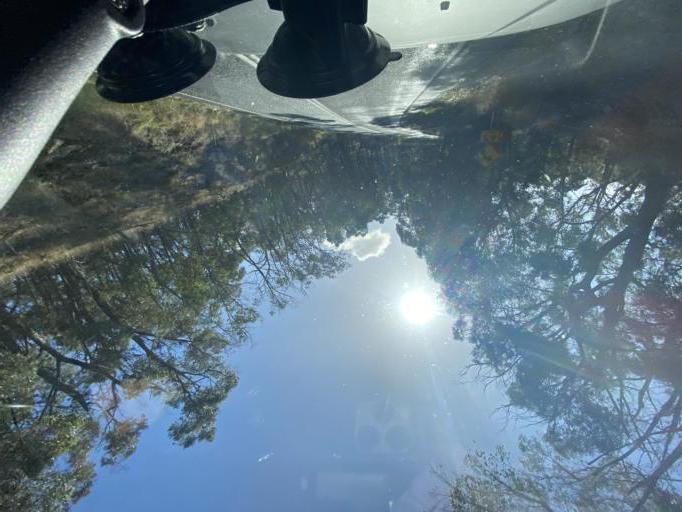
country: AU
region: Victoria
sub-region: Murrindindi
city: Kinglake West
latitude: -37.3013
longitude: 145.3696
